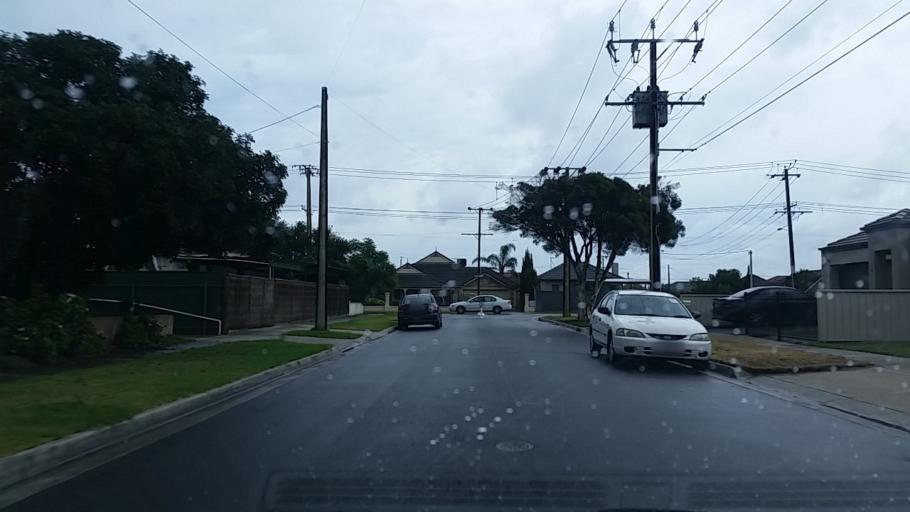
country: AU
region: South Australia
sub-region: Charles Sturt
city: Seaton
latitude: -34.8940
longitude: 138.5188
